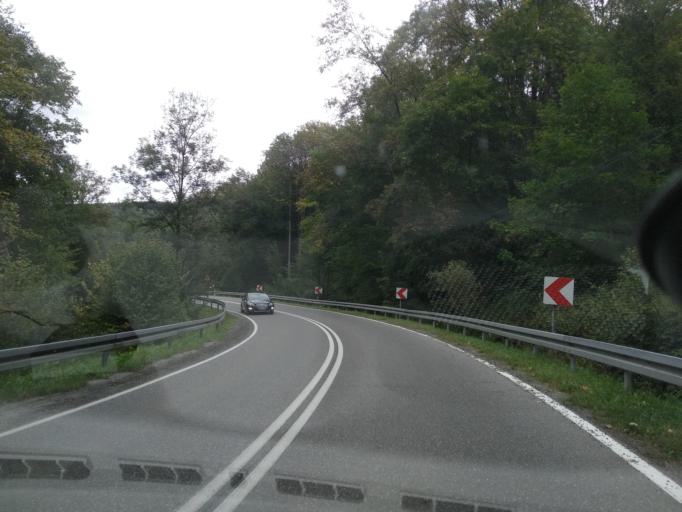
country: PL
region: Lesser Poland Voivodeship
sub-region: Powiat gorlicki
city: Sekowa
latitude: 49.5851
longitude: 21.2399
